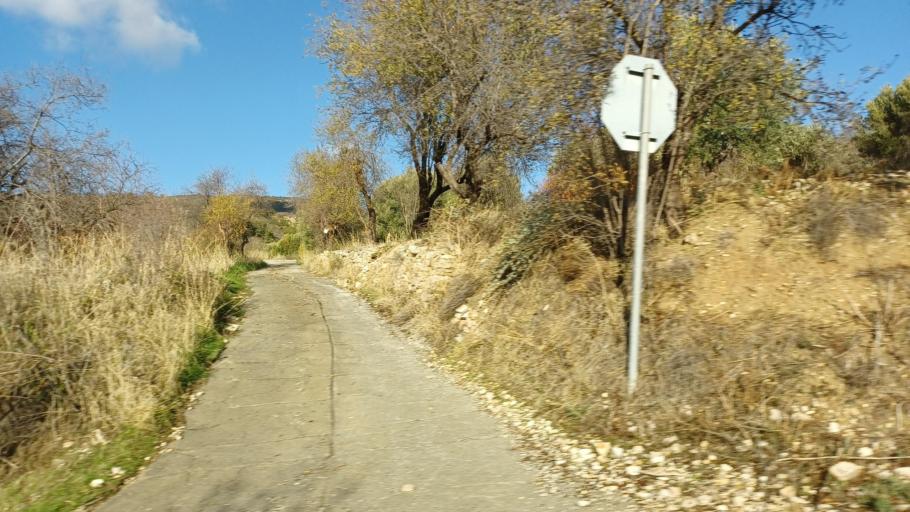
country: CY
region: Limassol
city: Pachna
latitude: 34.8577
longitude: 32.7220
